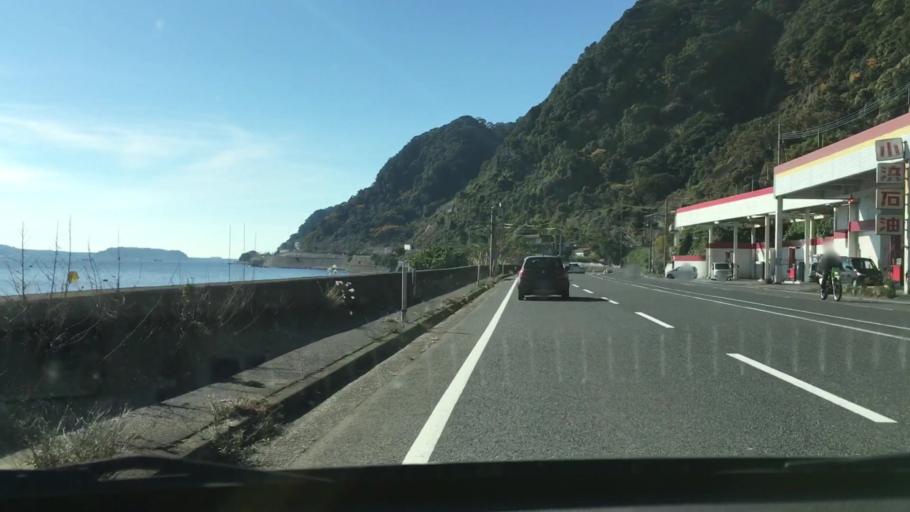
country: JP
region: Kagoshima
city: Kagoshima-shi
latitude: 31.6471
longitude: 130.6045
